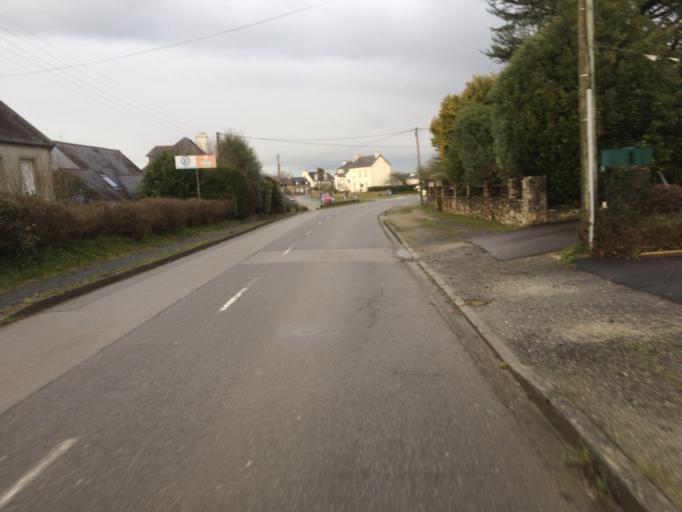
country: FR
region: Brittany
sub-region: Departement du Finistere
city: Logonna-Daoulas
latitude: 48.3262
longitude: -4.2969
